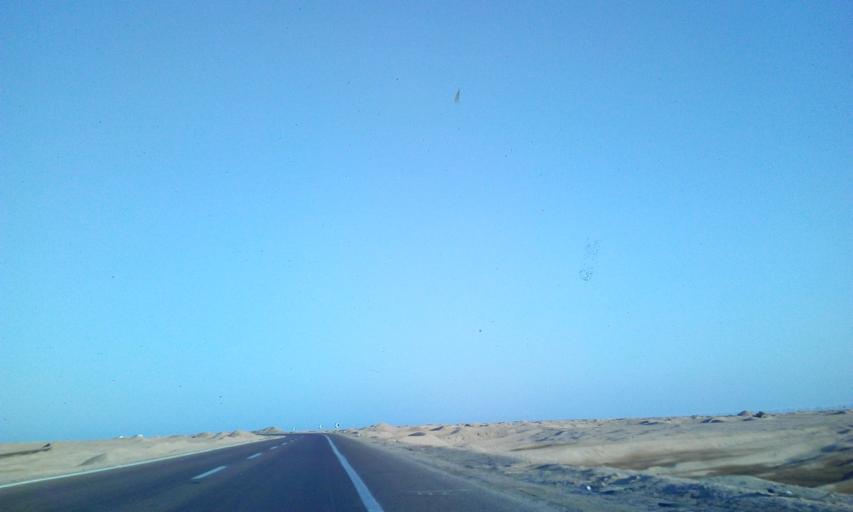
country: EG
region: South Sinai
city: Tor
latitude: 28.2765
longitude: 33.1262
